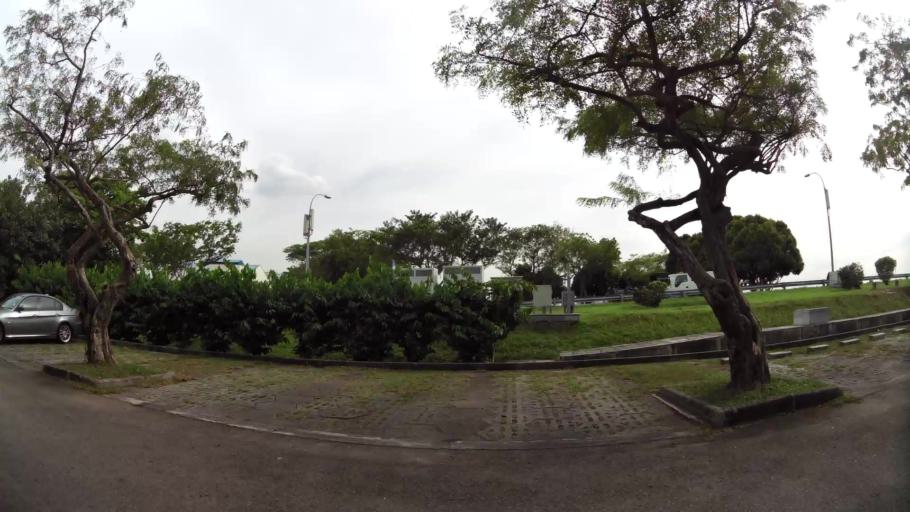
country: MY
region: Johor
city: Johor Bahru
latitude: 1.4389
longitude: 103.7426
